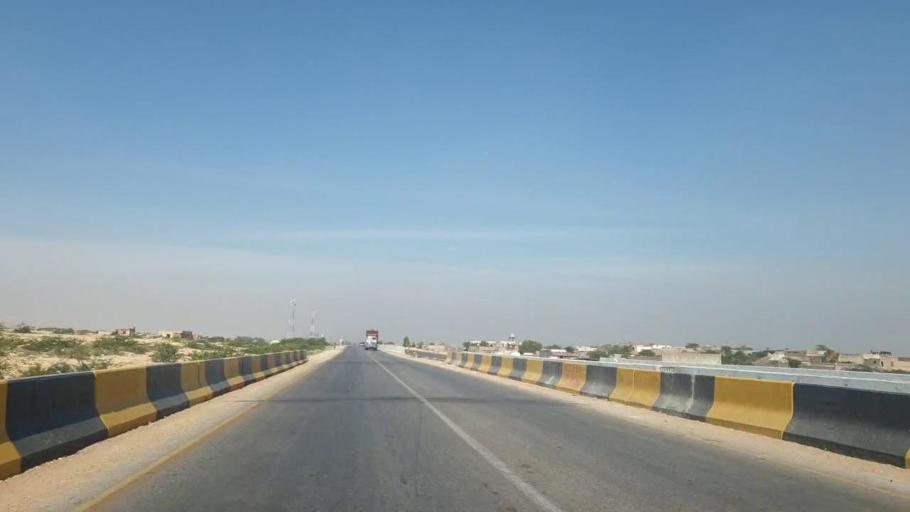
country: PK
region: Sindh
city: Hala
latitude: 25.6959
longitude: 68.2955
